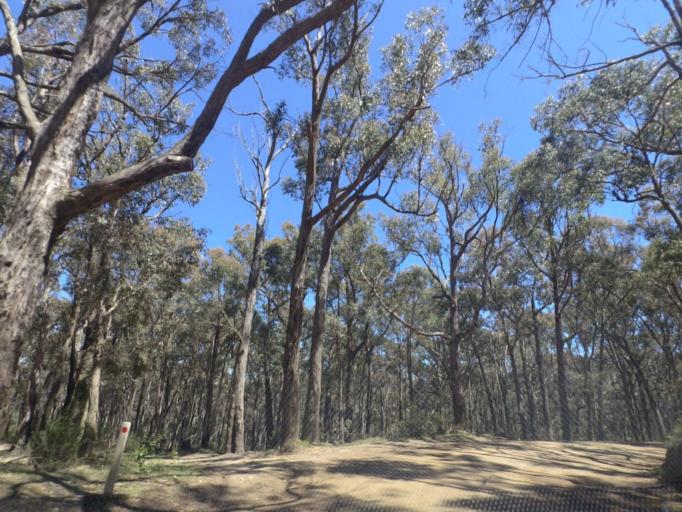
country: AU
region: Victoria
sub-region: Hume
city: Sunbury
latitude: -37.3916
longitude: 144.5654
